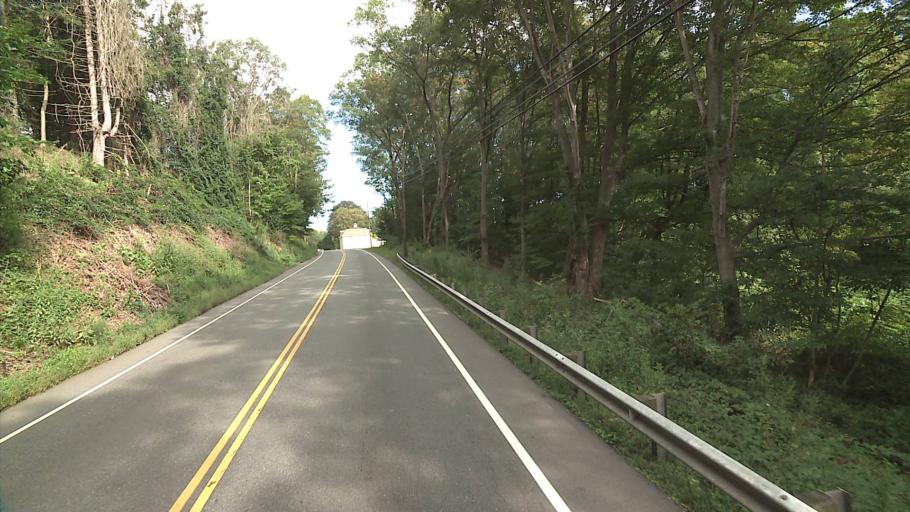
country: US
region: Connecticut
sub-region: New London County
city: Baltic
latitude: 41.6000
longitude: -72.1320
